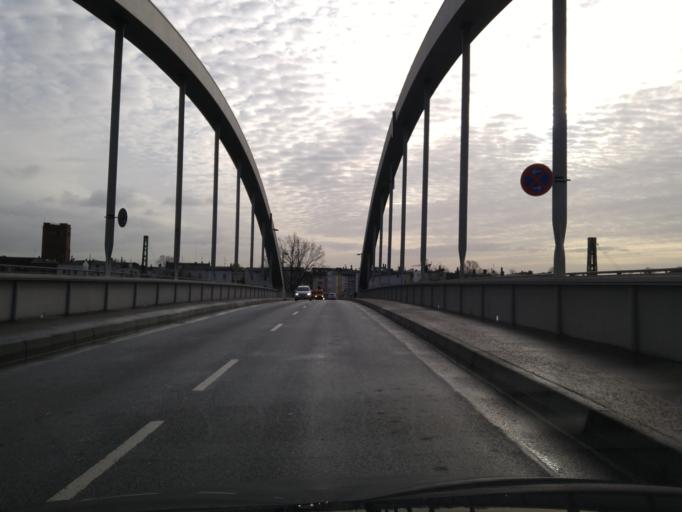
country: DE
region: Schleswig-Holstein
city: Luebeck
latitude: 53.8661
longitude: 10.6650
